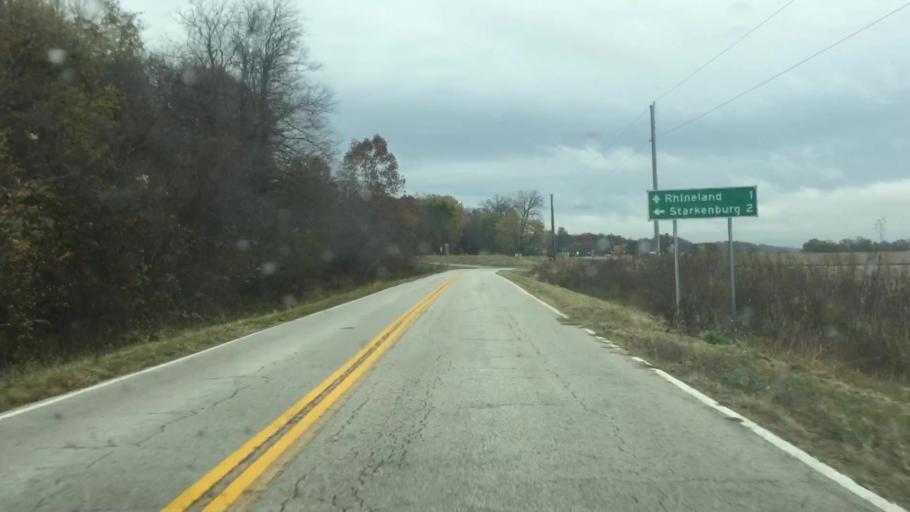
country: US
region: Missouri
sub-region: Gasconade County
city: Hermann
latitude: 38.7126
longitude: -91.5334
